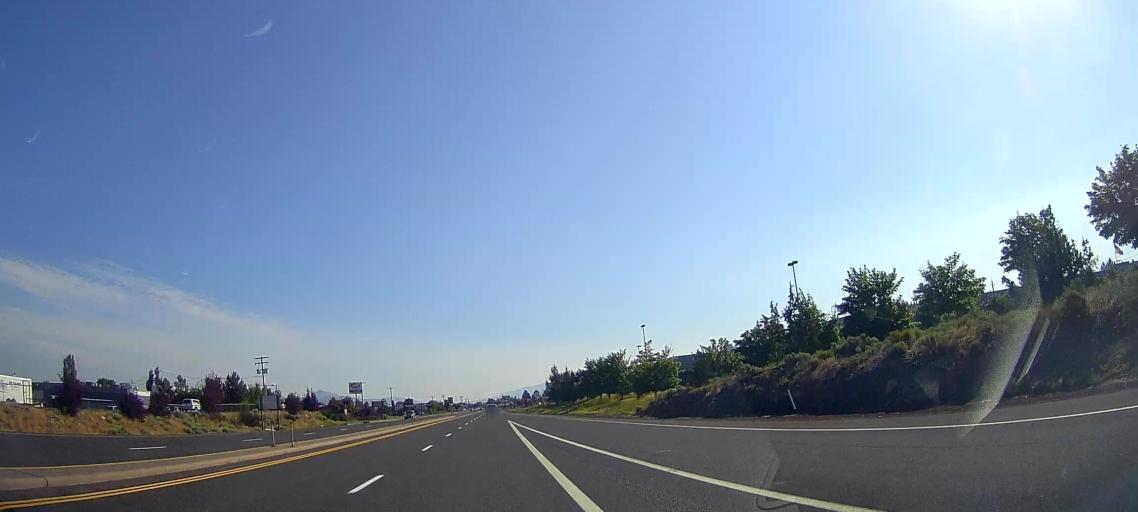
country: US
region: Oregon
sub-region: Deschutes County
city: Redmond
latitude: 44.2442
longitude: -121.1912
